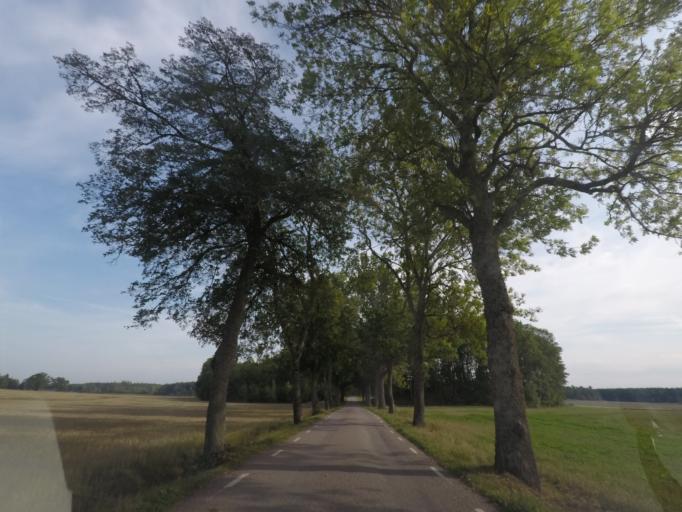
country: SE
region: Vaestmanland
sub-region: Kungsors Kommun
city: Kungsoer
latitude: 59.4874
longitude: 16.1744
